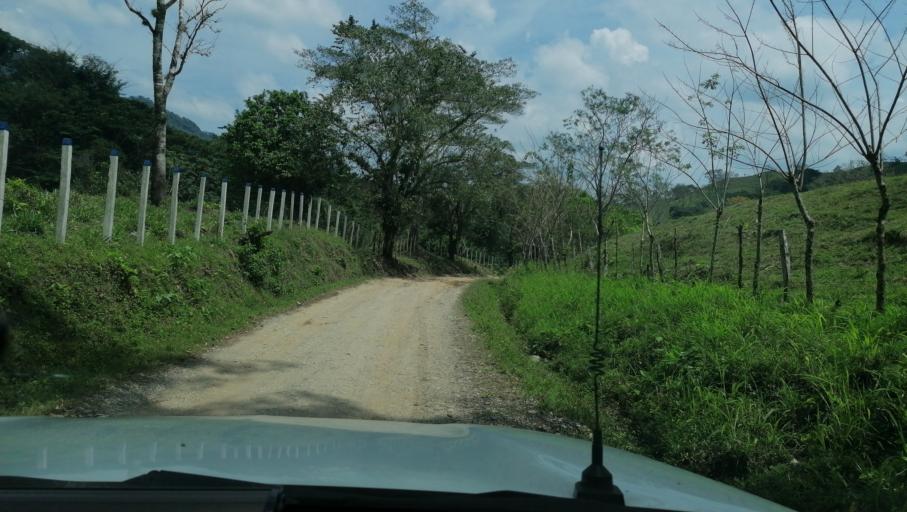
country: MX
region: Chiapas
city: Ixtacomitan
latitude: 17.4445
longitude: -93.1765
